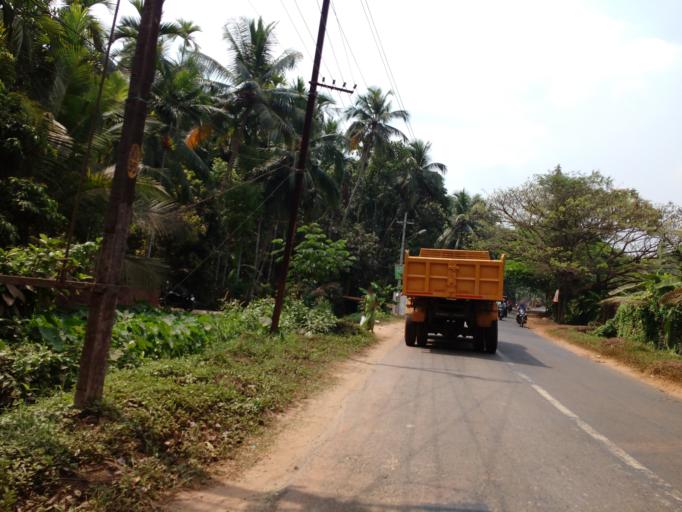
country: IN
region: Kerala
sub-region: Kozhikode
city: Kunnamangalam
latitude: 11.2897
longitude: 75.8617
